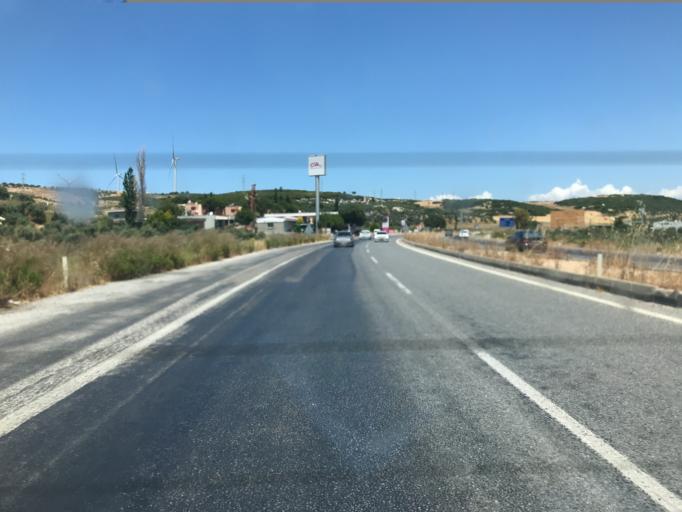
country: TR
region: Aydin
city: Akkoy
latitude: 37.4799
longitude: 27.3394
